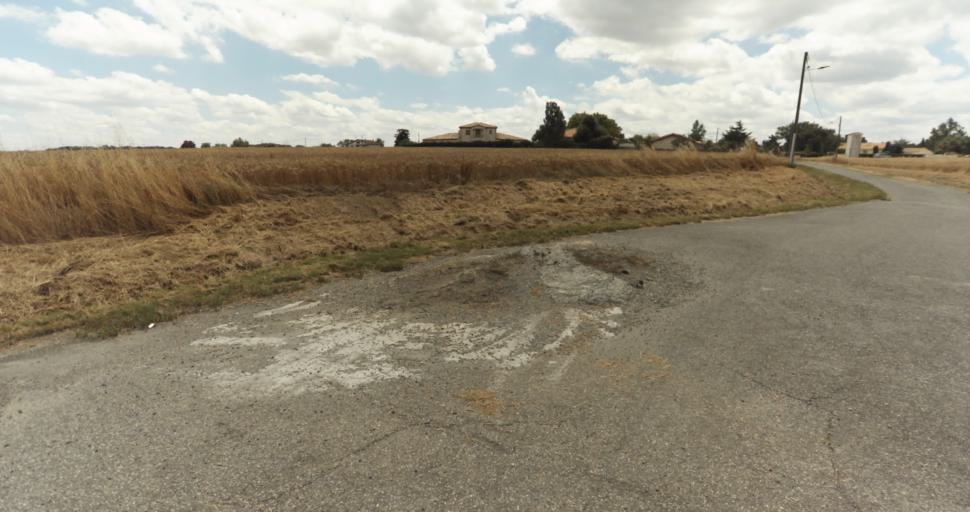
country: FR
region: Midi-Pyrenees
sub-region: Departement de la Haute-Garonne
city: Fontenilles
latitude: 43.5473
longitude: 1.1867
